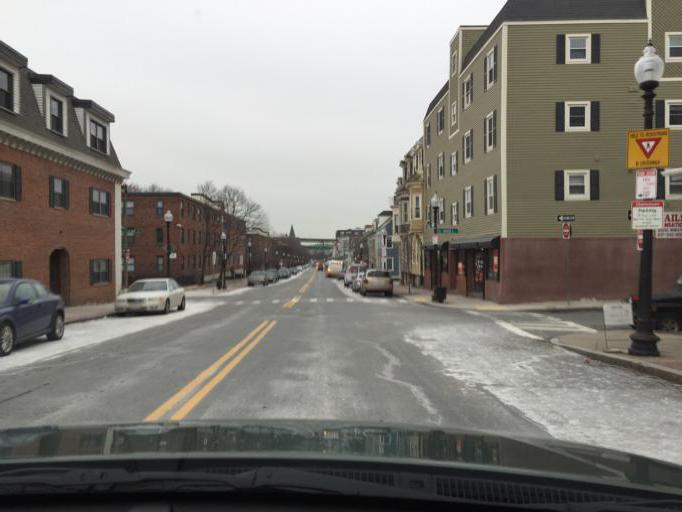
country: US
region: Massachusetts
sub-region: Suffolk County
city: Boston
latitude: 42.3788
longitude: -71.0620
